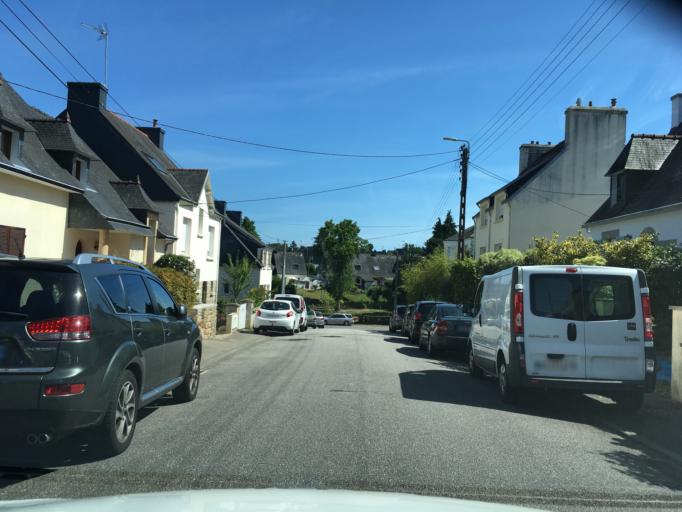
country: FR
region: Brittany
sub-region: Departement du Finistere
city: Quimper
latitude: 47.9744
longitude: -4.1193
